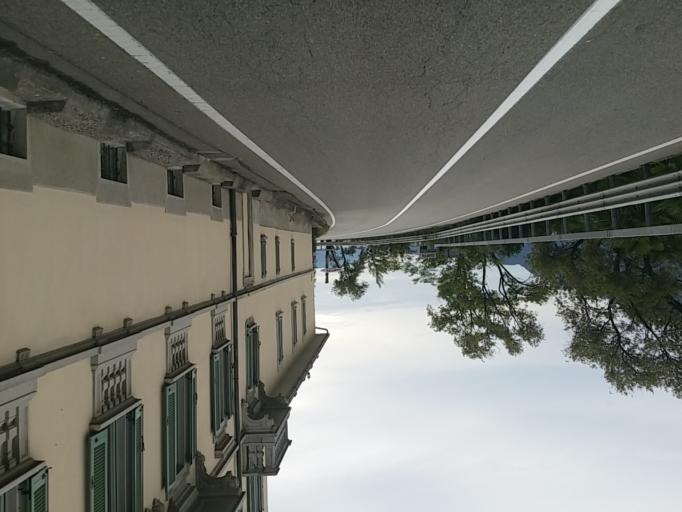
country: IT
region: Piedmont
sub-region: Provincia Verbano-Cusio-Ossola
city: Oggebbio
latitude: 45.9779
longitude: 8.6351
